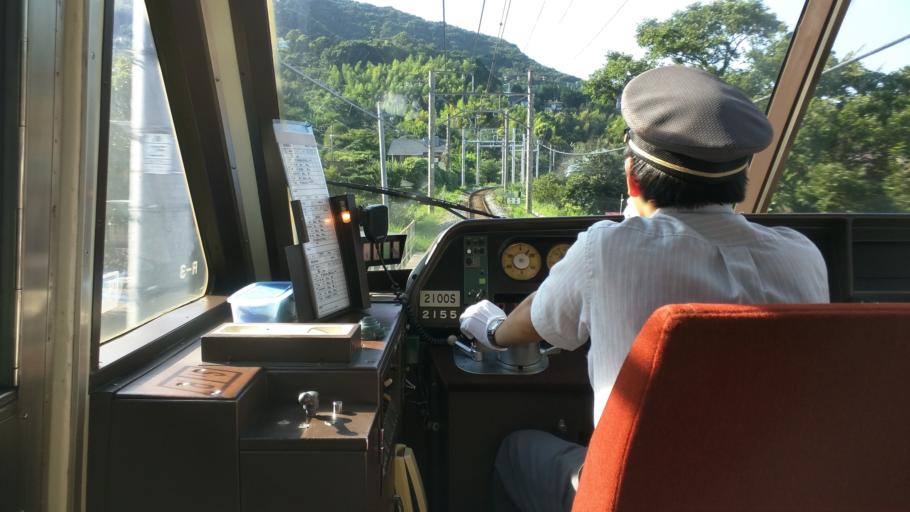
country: JP
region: Shizuoka
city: Atami
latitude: 35.0489
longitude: 139.0672
